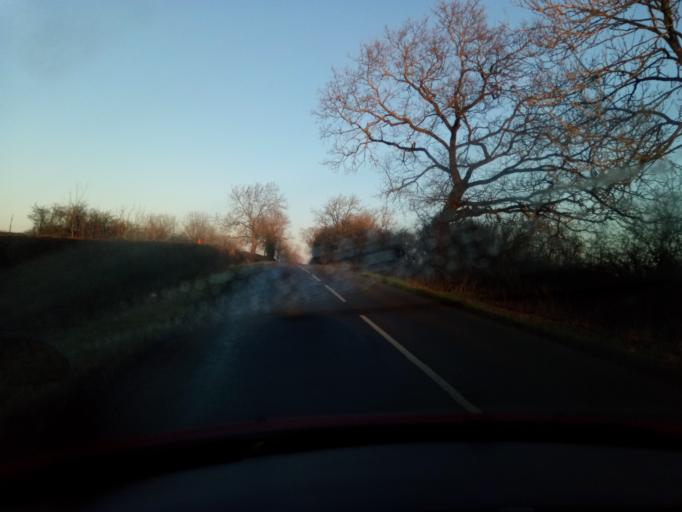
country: GB
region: England
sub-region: Leicestershire
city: Sileby
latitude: 52.7540
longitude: -1.0939
